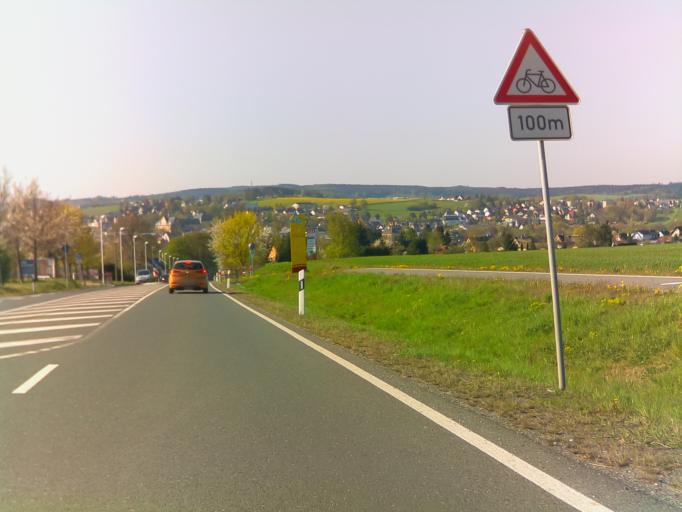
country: DE
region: Thuringia
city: Schleiz
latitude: 50.5889
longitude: 11.8122
